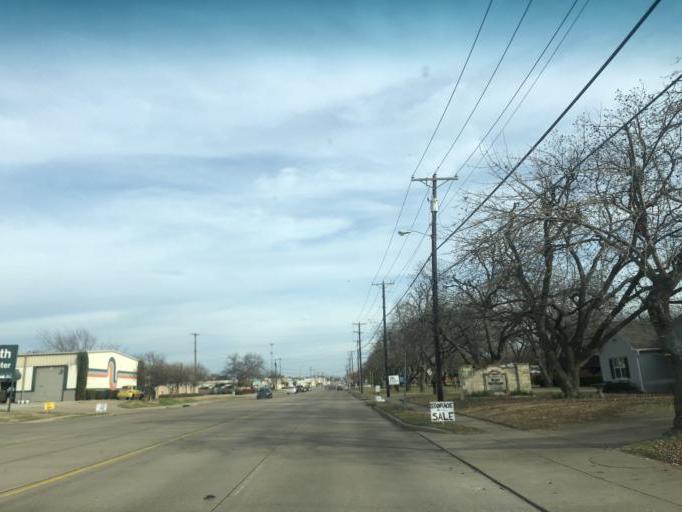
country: US
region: Texas
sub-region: Tarrant County
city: Dalworthington Gardens
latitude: 32.7068
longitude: -97.1523
